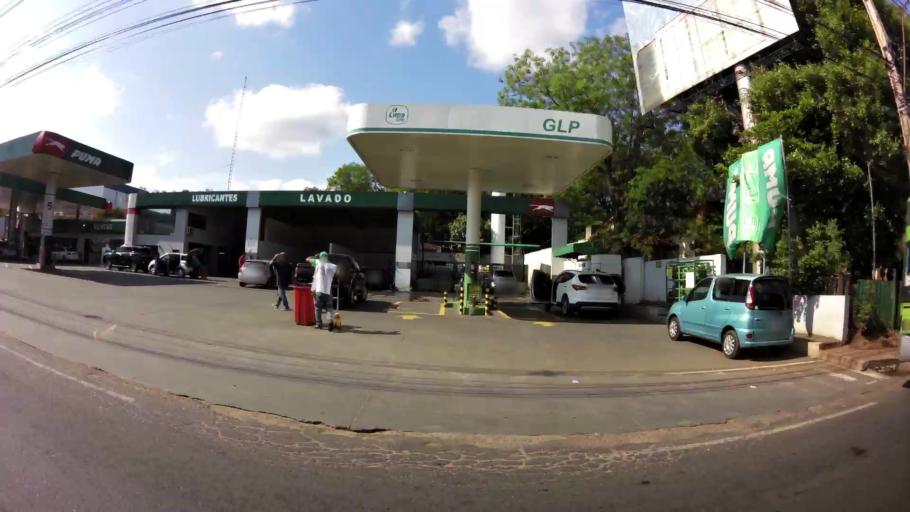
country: PY
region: Central
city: Fernando de la Mora
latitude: -25.3349
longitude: -57.5341
